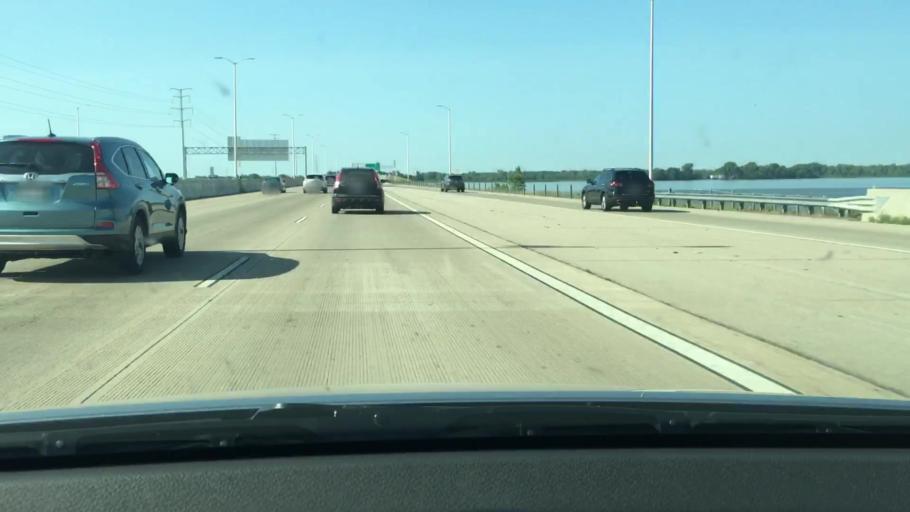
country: US
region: Wisconsin
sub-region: Winnebago County
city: Oshkosh
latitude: 44.0526
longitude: -88.5767
